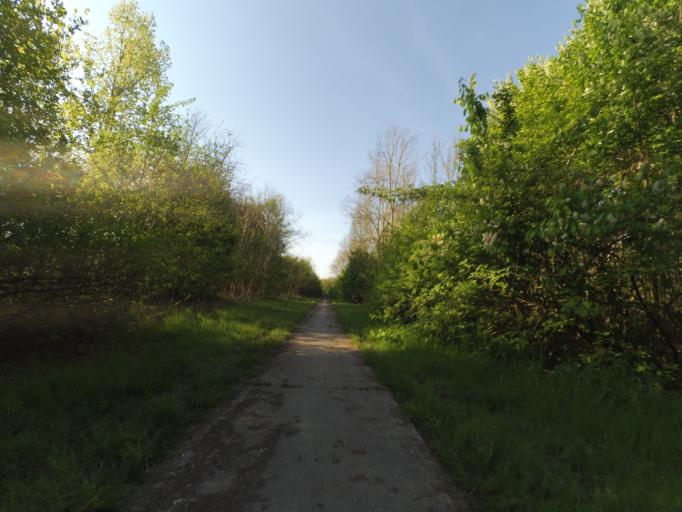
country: NL
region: Flevoland
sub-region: Gemeente Almere
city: Almere Stad
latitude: 52.3966
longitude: 5.3300
